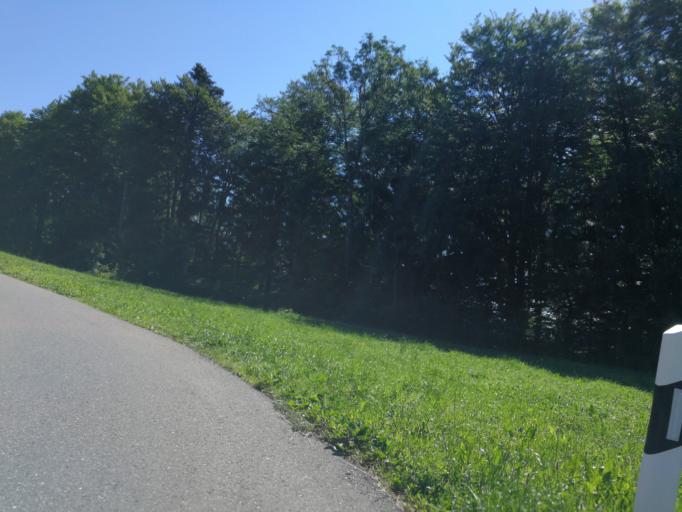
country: CH
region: Zurich
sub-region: Bezirk Hinwil
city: Wald
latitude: 47.2894
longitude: 8.8875
